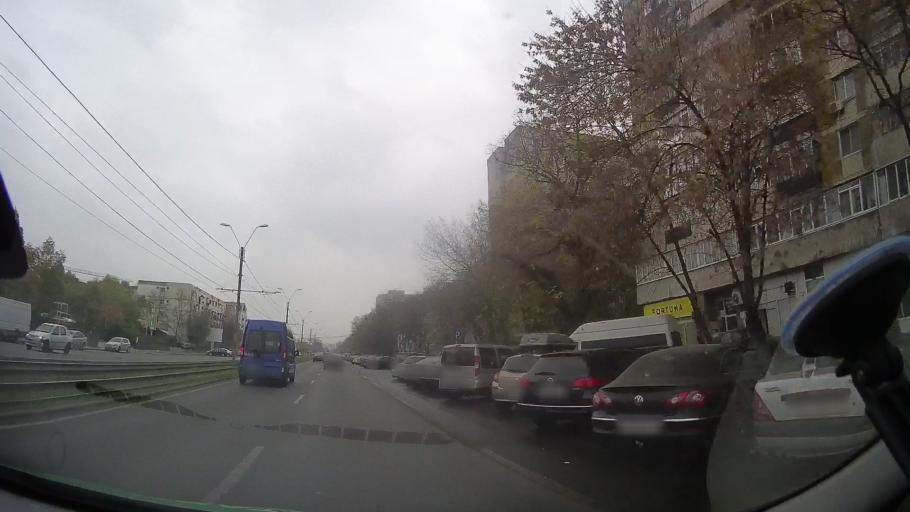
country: RO
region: Ilfov
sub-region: Comuna Chiajna
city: Rosu
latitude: 44.4265
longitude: 26.0229
